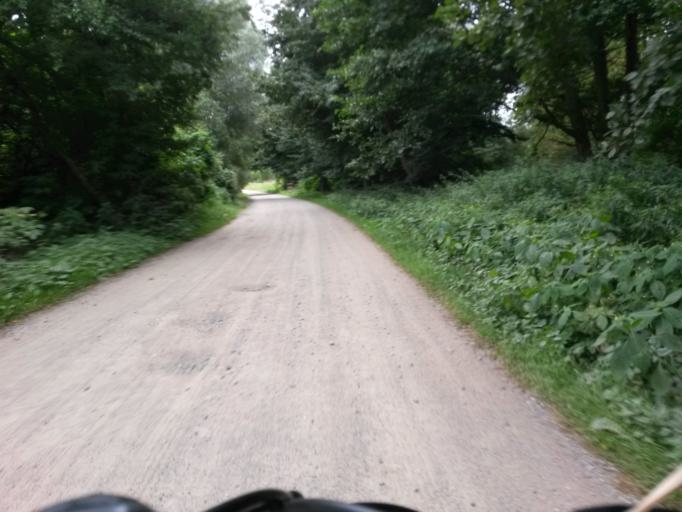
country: DE
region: Brandenburg
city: Angermunde
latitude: 53.0351
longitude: 13.9502
